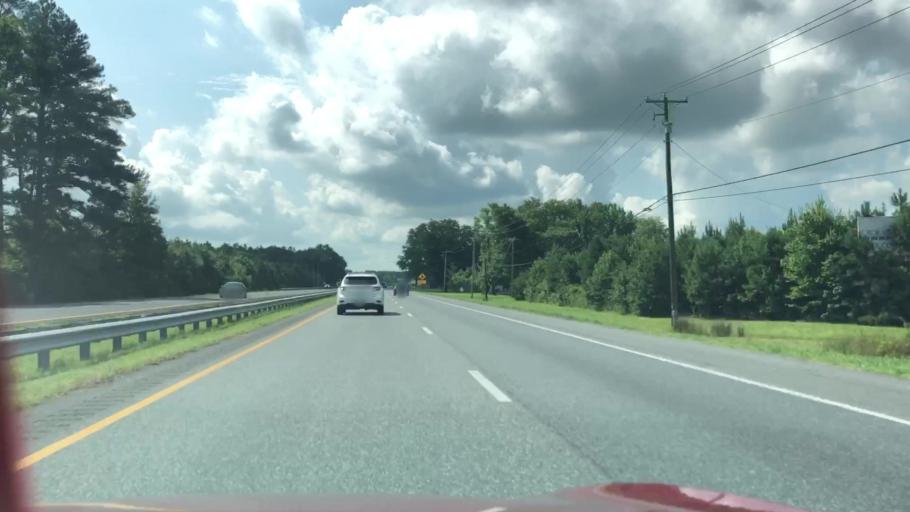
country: US
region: Maryland
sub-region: Worcester County
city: Pocomoke City
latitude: 38.0384
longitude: -75.5422
